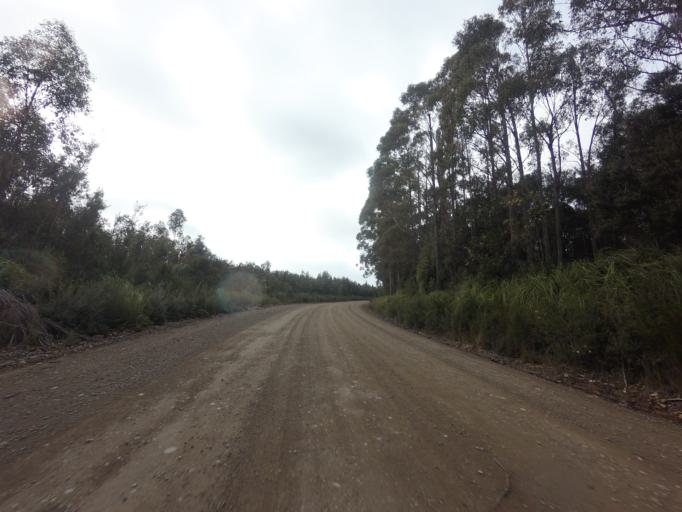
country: AU
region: Tasmania
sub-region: Huon Valley
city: Geeveston
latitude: -43.5084
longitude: 146.8816
